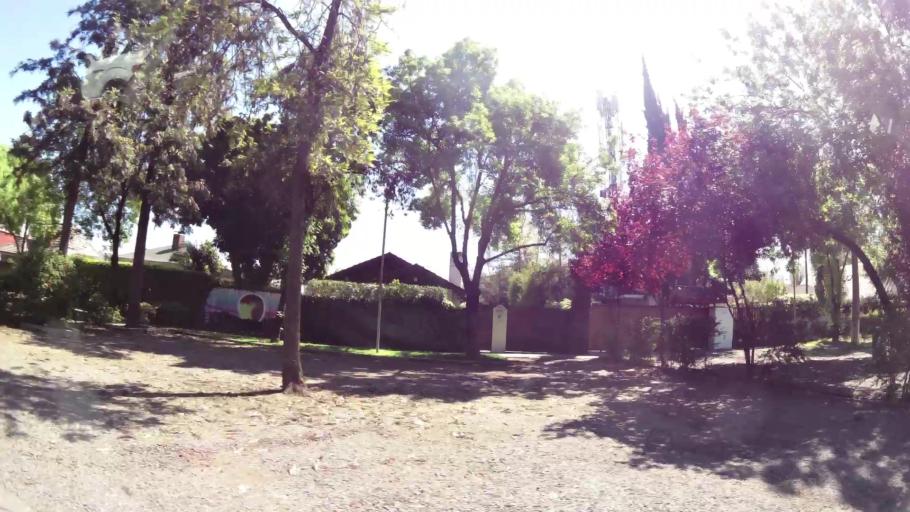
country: CL
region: Santiago Metropolitan
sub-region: Provincia de Santiago
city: Villa Presidente Frei, Nunoa, Santiago, Chile
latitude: -33.4135
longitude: -70.5484
